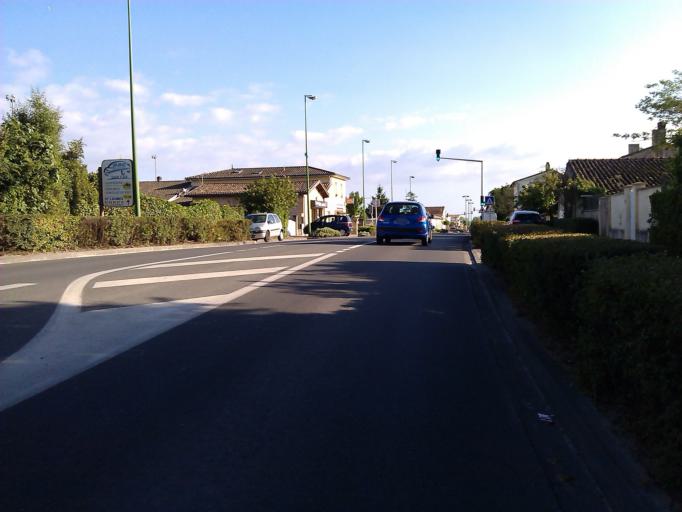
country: FR
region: Aquitaine
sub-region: Departement de la Gironde
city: Cubzac-les-Ponts
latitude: 44.9735
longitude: -0.4523
